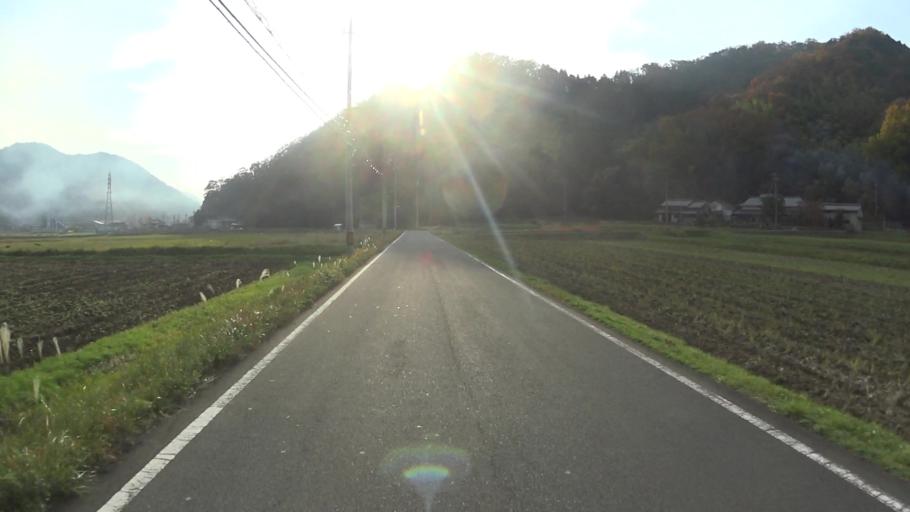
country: JP
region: Kyoto
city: Maizuru
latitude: 35.5202
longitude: 135.4046
